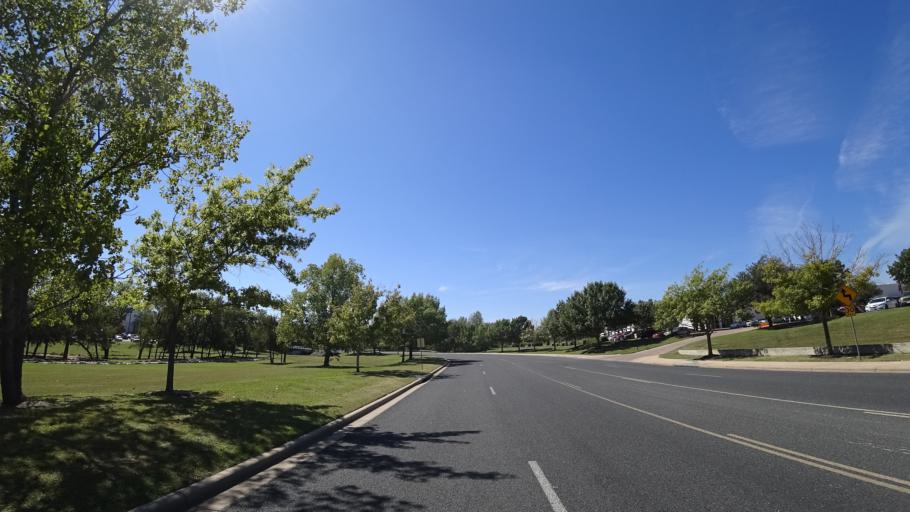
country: US
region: Texas
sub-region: Travis County
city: Austin
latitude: 30.2148
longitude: -97.6933
